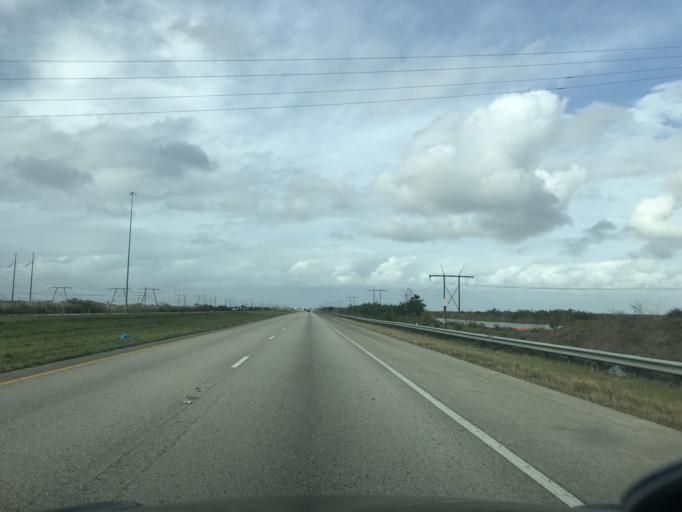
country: US
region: Florida
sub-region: Broward County
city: Weston
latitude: 26.1496
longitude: -80.4426
